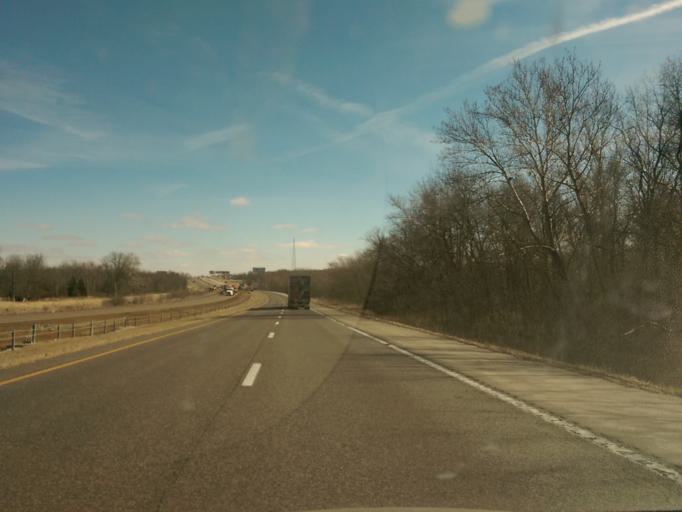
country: US
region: Missouri
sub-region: Boone County
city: Hallsville
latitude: 38.9550
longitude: -92.1570
